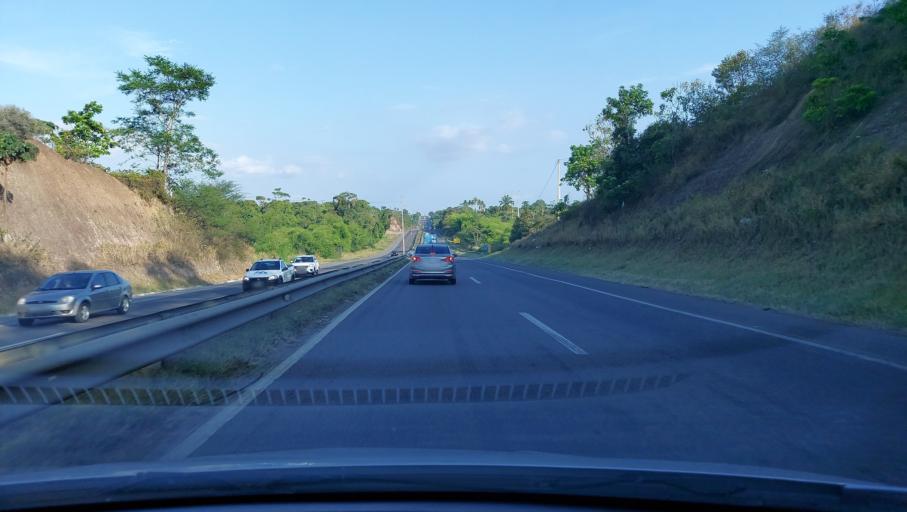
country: BR
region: Bahia
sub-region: Conceicao Do Jacuipe
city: Conceicao do Jacuipe
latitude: -12.3918
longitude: -38.7810
